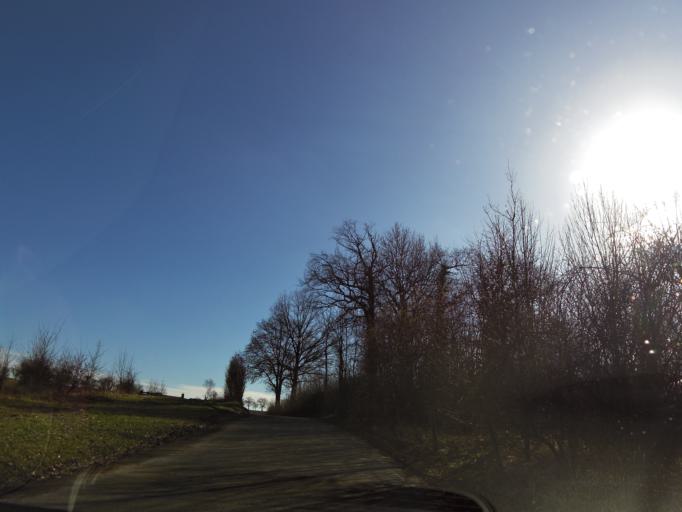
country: NL
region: Limburg
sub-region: Valkenburg aan de Geul
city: Schin op Geul
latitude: 50.8038
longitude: 5.8840
